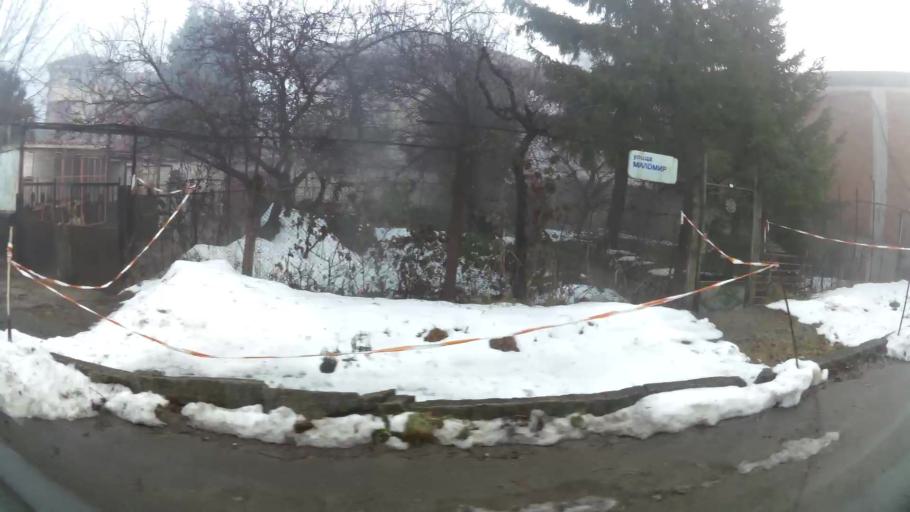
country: BG
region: Sofia-Capital
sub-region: Stolichna Obshtina
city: Sofia
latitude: 42.6536
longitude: 23.2647
